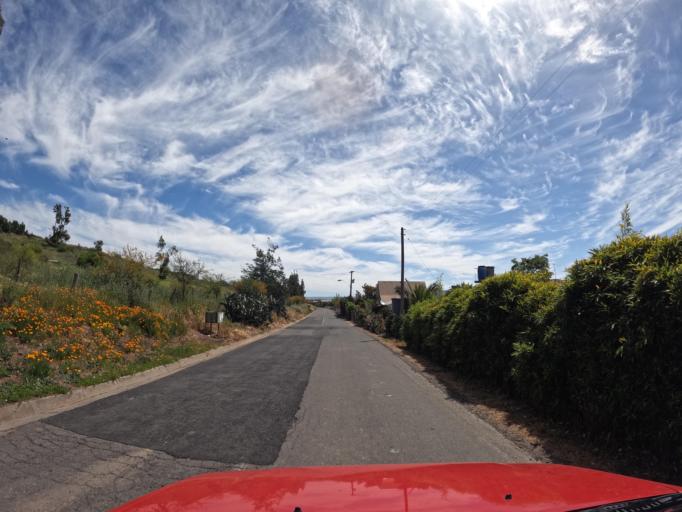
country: CL
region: Maule
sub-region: Provincia de Talca
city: Talca
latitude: -34.9893
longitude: -71.8422
